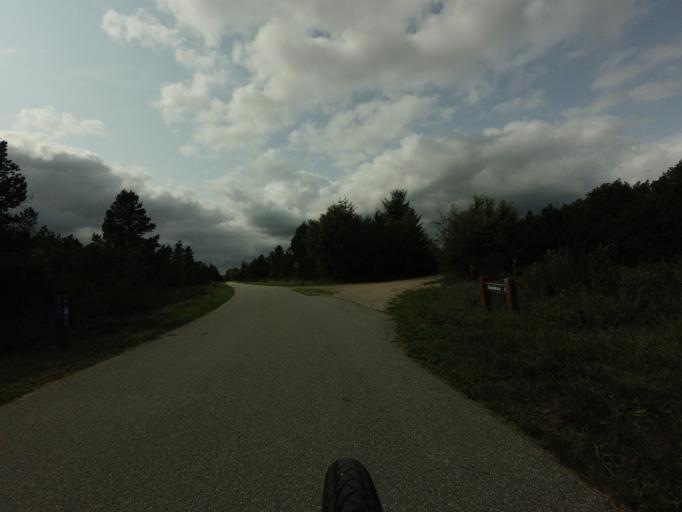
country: DK
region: North Denmark
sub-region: Frederikshavn Kommune
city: Strandby
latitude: 57.6414
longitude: 10.4220
